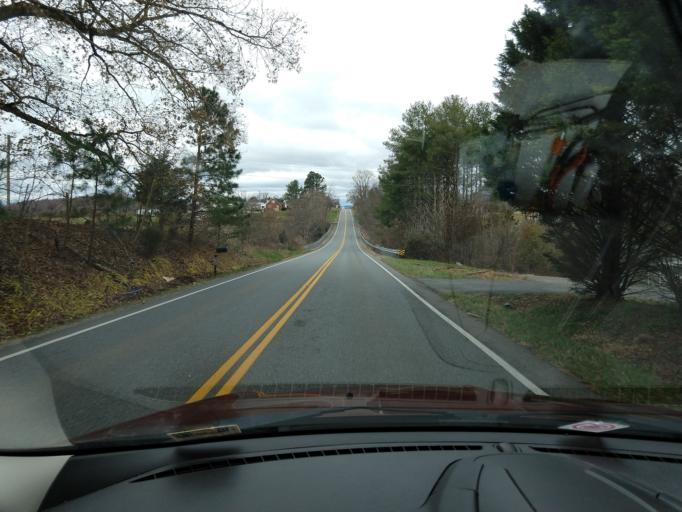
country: US
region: Virginia
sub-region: Botetourt County
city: Blue Ridge
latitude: 37.2531
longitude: -79.7074
